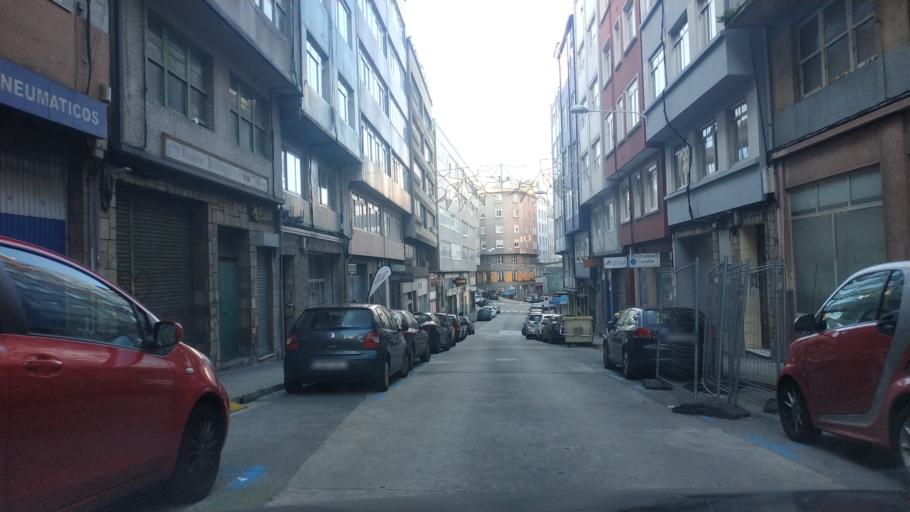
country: ES
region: Galicia
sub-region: Provincia da Coruna
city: A Coruna
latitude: 43.3601
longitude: -8.4080
